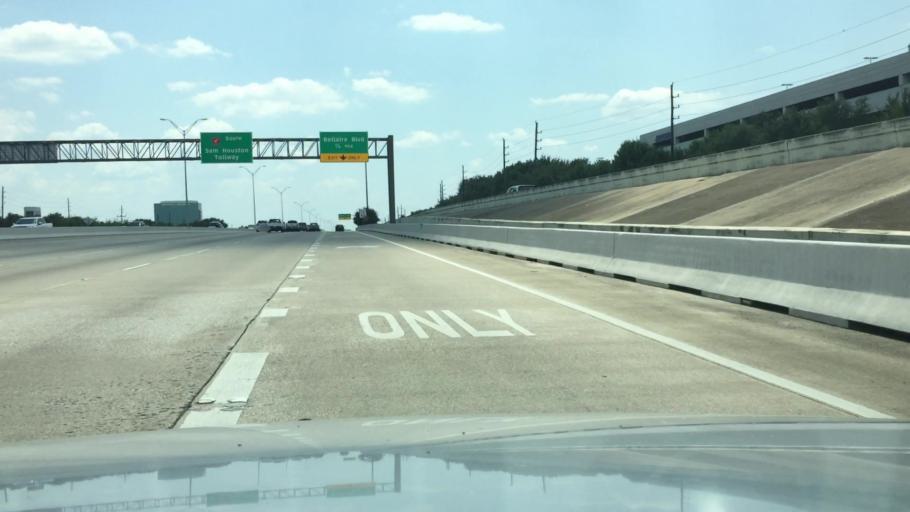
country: US
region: Texas
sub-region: Harris County
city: Bunker Hill Village
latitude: 29.7149
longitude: -95.5576
